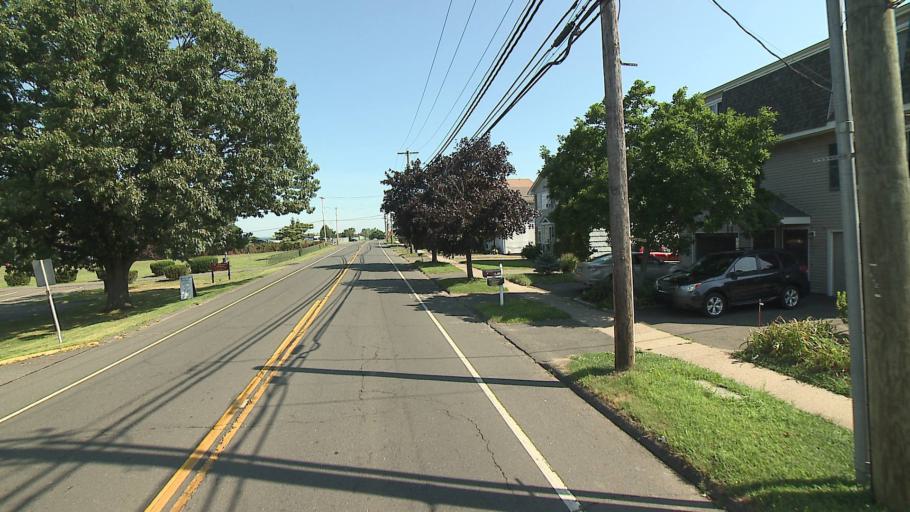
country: US
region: Connecticut
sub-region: Fairfield County
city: Stratford
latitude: 41.1616
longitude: -73.1176
